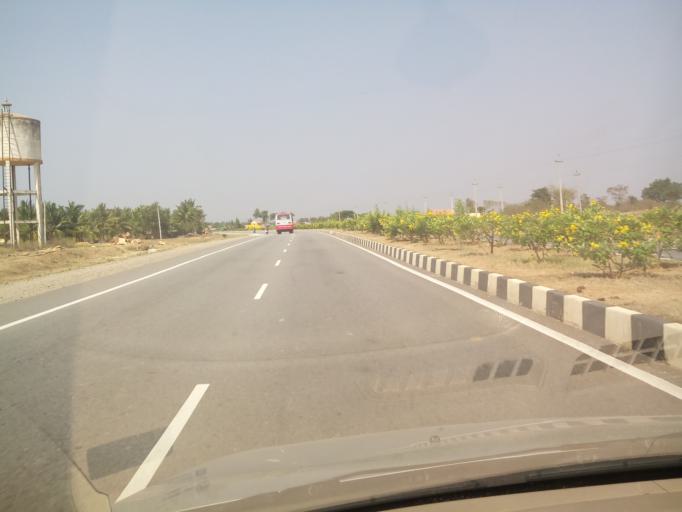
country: IN
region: Karnataka
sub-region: Hassan
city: Shravanabelagola
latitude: 12.9192
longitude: 76.4712
